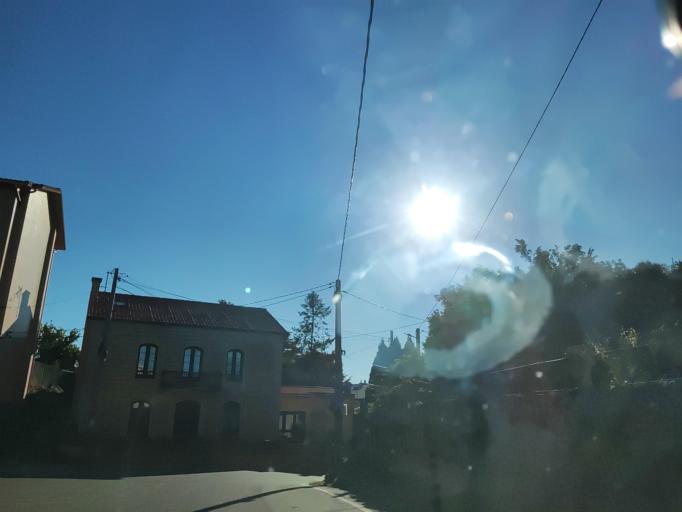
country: ES
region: Galicia
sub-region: Provincia da Coruna
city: Boiro
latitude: 42.5949
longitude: -8.9322
